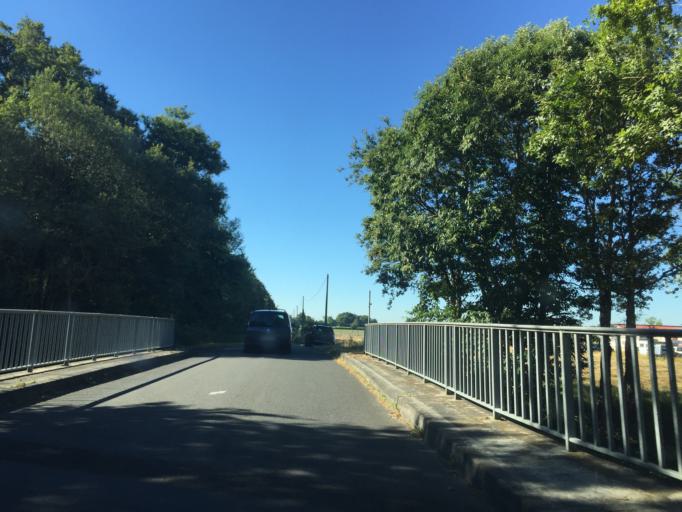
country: FR
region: Auvergne
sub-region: Departement de l'Allier
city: Dompierre-sur-Besbre
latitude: 46.5264
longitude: 3.6200
